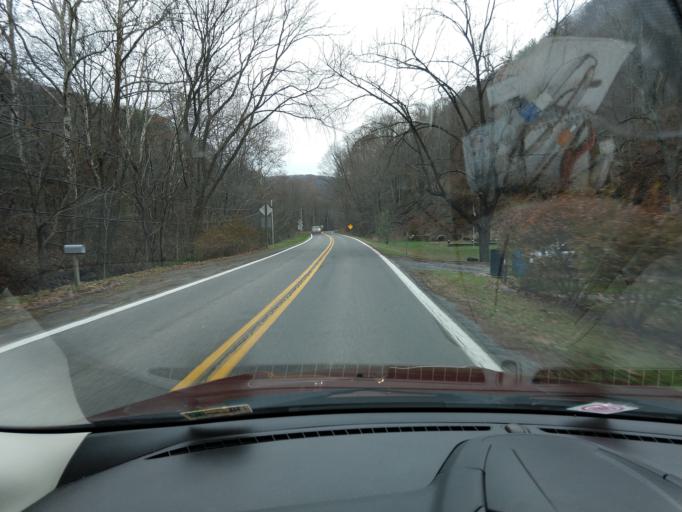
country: US
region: West Virginia
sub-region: Greenbrier County
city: White Sulphur Springs
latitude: 37.7460
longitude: -80.2392
